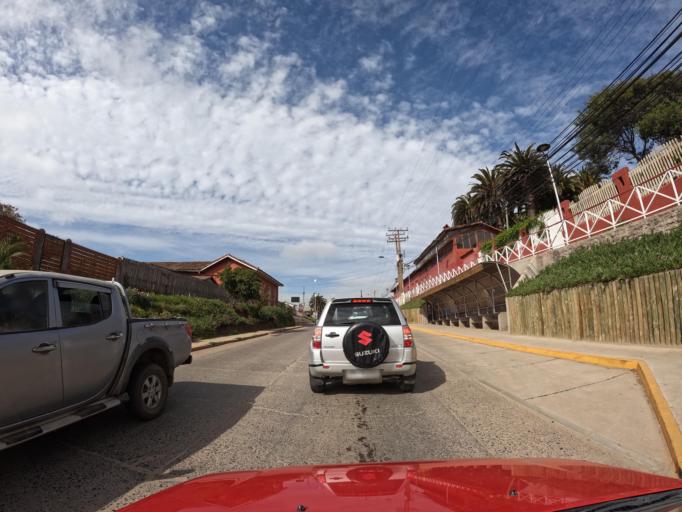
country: CL
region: O'Higgins
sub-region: Provincia de Colchagua
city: Santa Cruz
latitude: -34.3871
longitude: -71.9983
